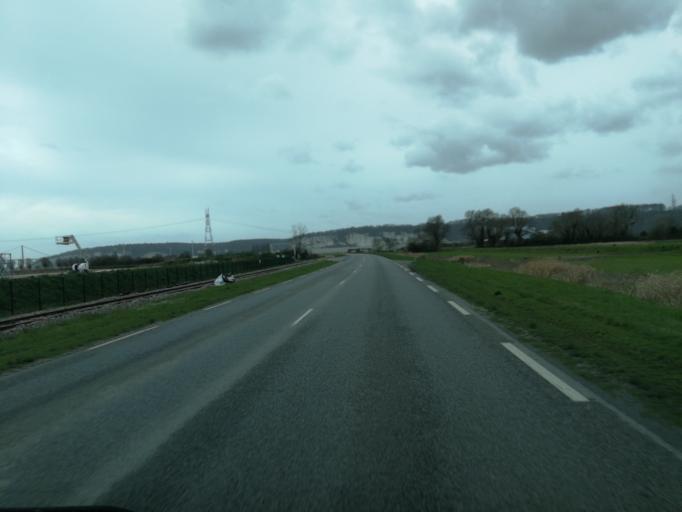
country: FR
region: Haute-Normandie
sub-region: Departement de l'Eure
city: Quillebeuf-sur-Seine
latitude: 49.4894
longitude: 0.5035
